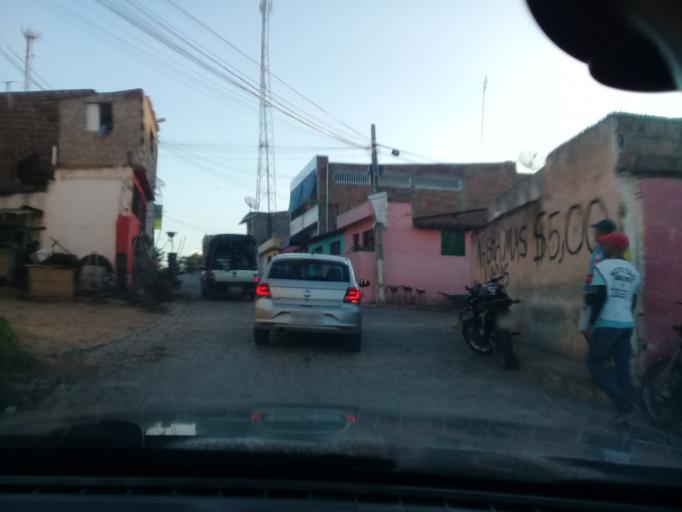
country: BR
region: Pernambuco
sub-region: Vitoria De Santo Antao
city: Vitoria de Santo Antao
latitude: -8.1289
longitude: -35.2866
